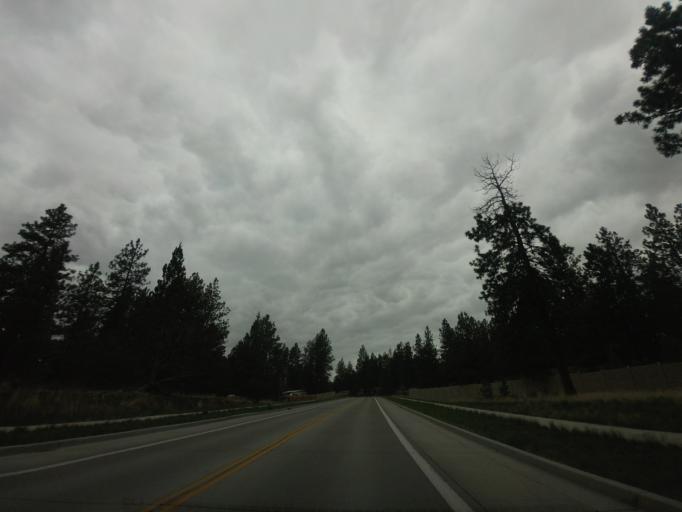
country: US
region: Oregon
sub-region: Deschutes County
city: Bend
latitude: 44.0187
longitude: -121.3239
